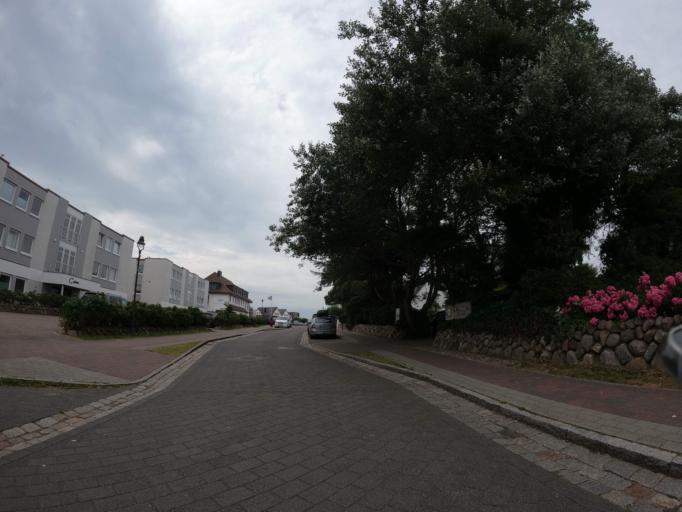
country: DE
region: Schleswig-Holstein
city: Westerland
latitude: 54.9361
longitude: 8.3224
